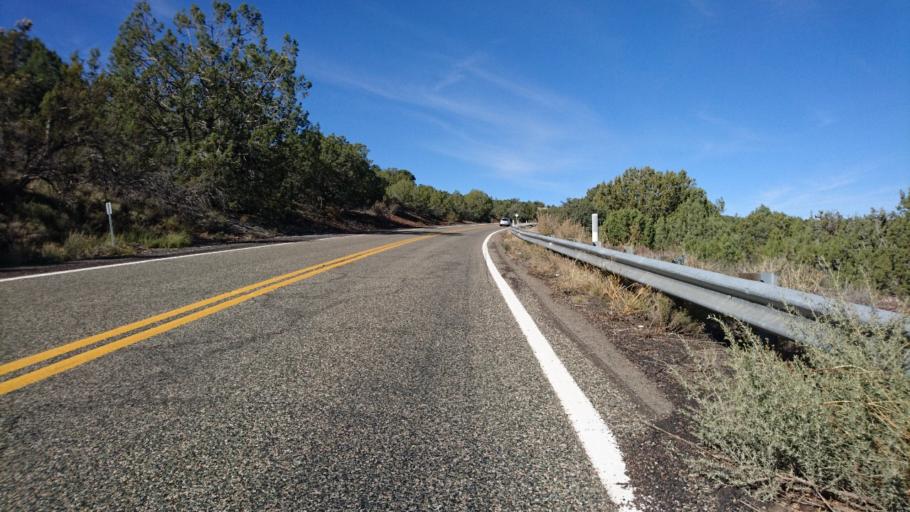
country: US
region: Arizona
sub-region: Yavapai County
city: Paulden
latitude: 35.2778
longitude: -112.6944
